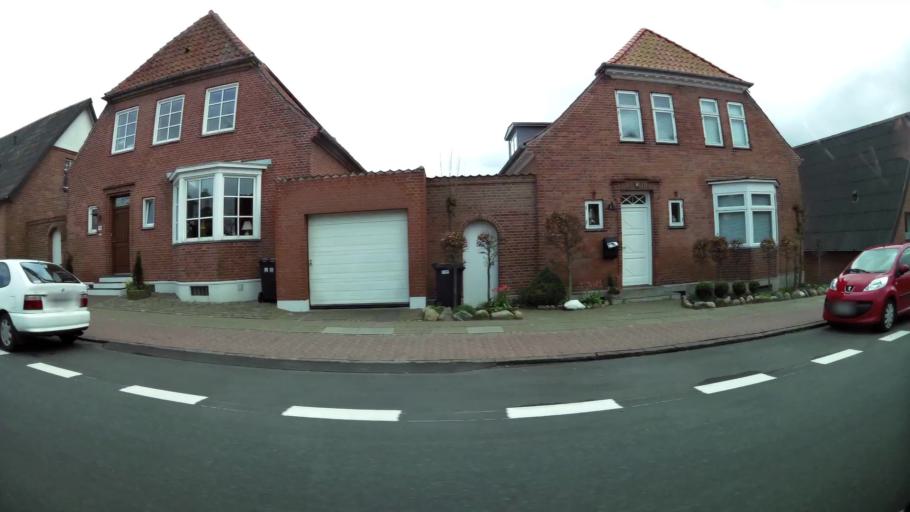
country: DK
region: North Denmark
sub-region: Thisted Kommune
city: Thisted
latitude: 56.9531
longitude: 8.6765
